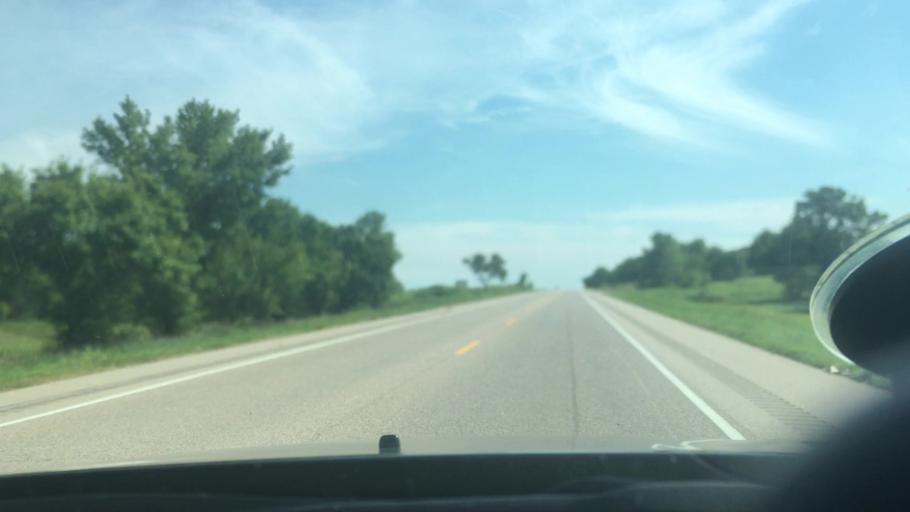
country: US
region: Oklahoma
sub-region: Seminole County
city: Seminole
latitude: 35.1610
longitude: -96.6744
